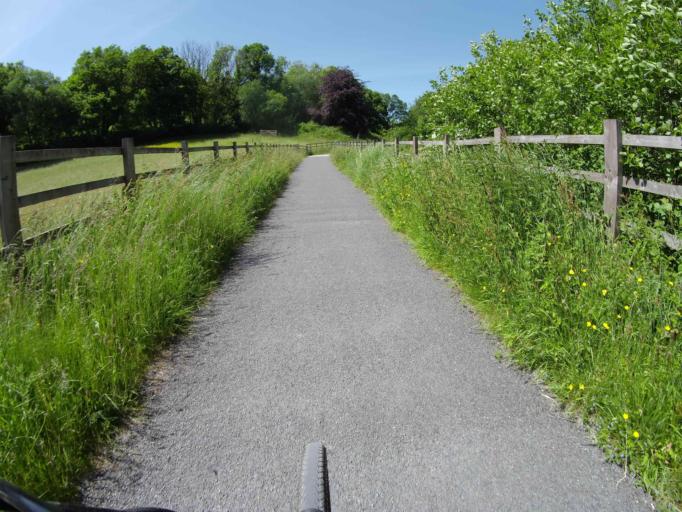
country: GB
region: England
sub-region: Devon
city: Bovey Tracey
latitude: 50.6522
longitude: -3.7460
